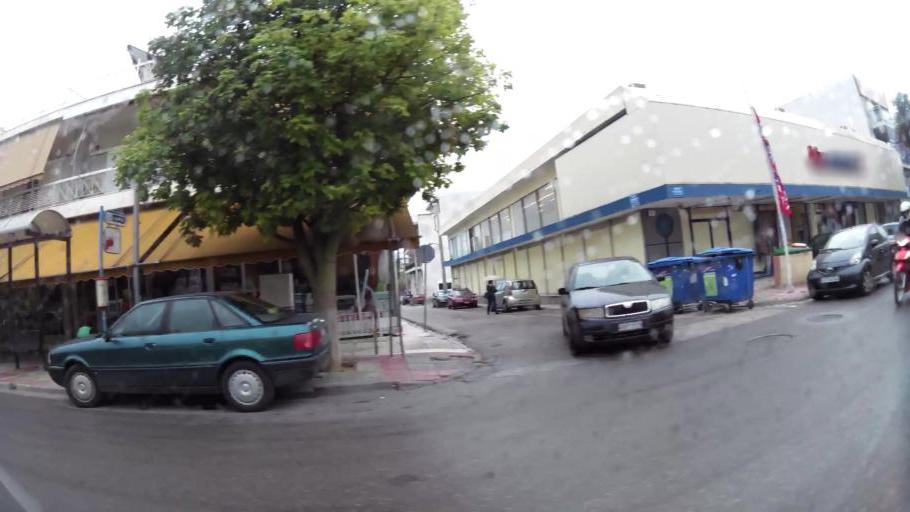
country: GR
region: Attica
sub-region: Nomarchia Athinas
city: Agioi Anargyroi
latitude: 38.0231
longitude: 23.7215
